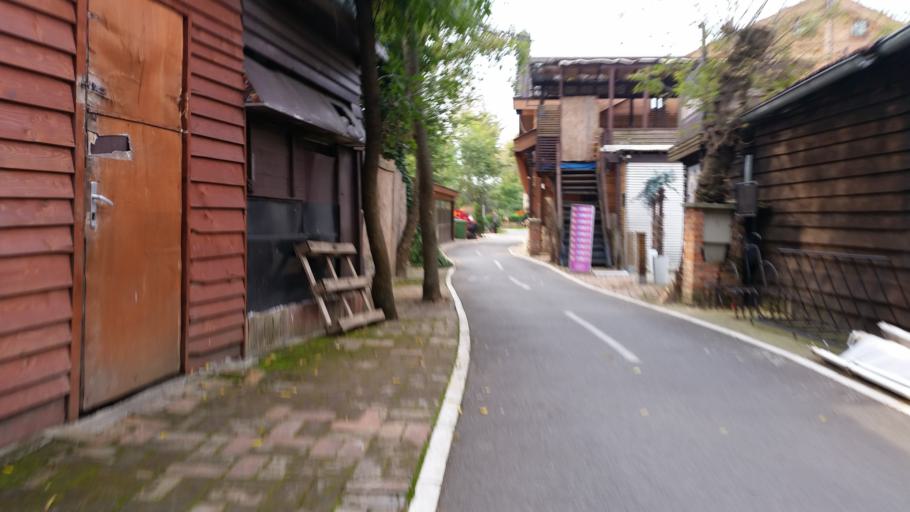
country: RS
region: Central Serbia
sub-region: Belgrade
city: Cukarica
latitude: 44.7823
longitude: 20.3904
